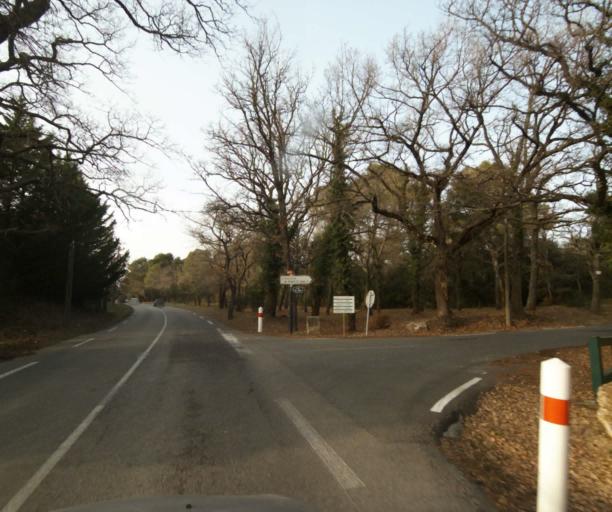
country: FR
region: Provence-Alpes-Cote d'Azur
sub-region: Departement des Bouches-du-Rhone
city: Eguilles
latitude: 43.6110
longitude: 5.3651
